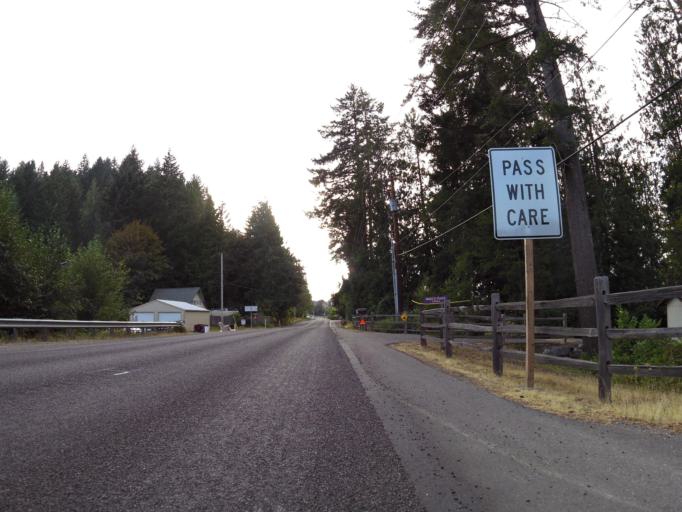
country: US
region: Washington
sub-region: Mason County
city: Allyn
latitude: 47.3815
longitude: -122.9493
